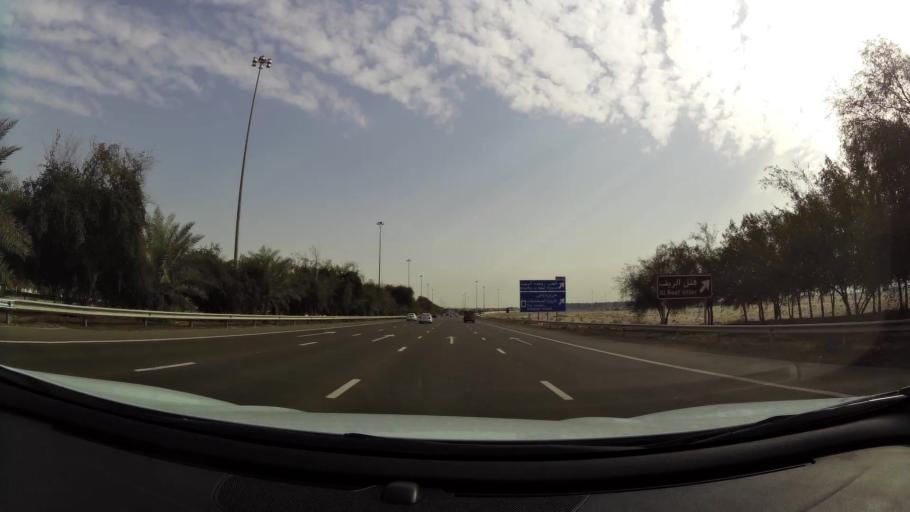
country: AE
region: Abu Dhabi
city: Abu Dhabi
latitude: 24.4702
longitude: 54.6763
